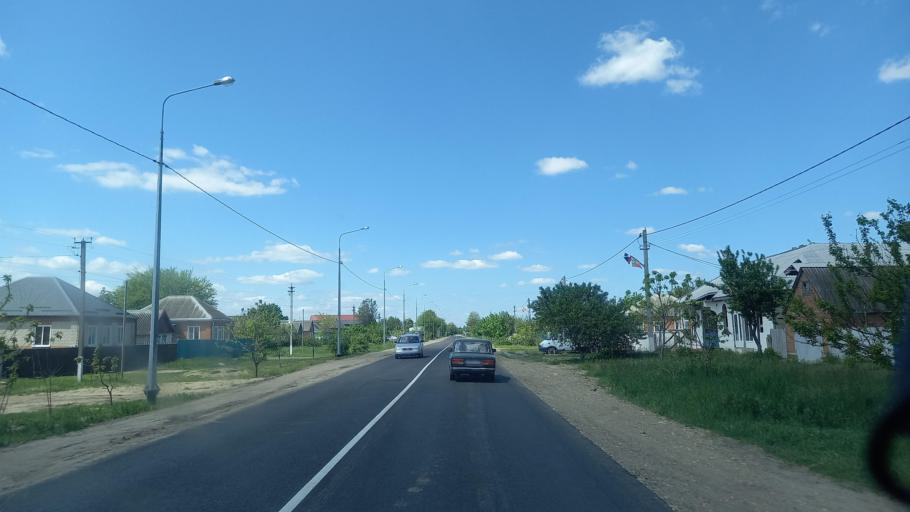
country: RU
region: Krasnodarskiy
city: Tbilisskaya
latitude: 45.3254
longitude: 40.2371
